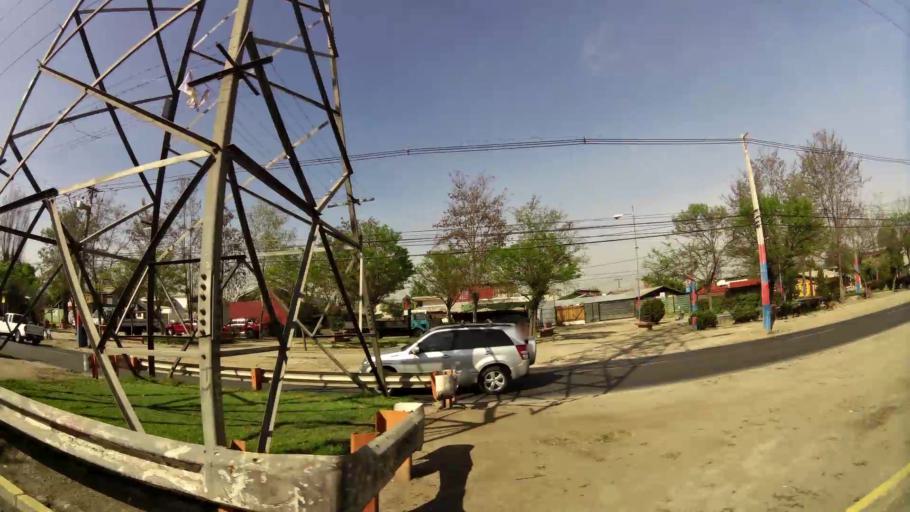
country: CL
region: Santiago Metropolitan
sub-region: Provincia de Santiago
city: Villa Presidente Frei, Nunoa, Santiago, Chile
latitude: -33.5023
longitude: -70.5761
